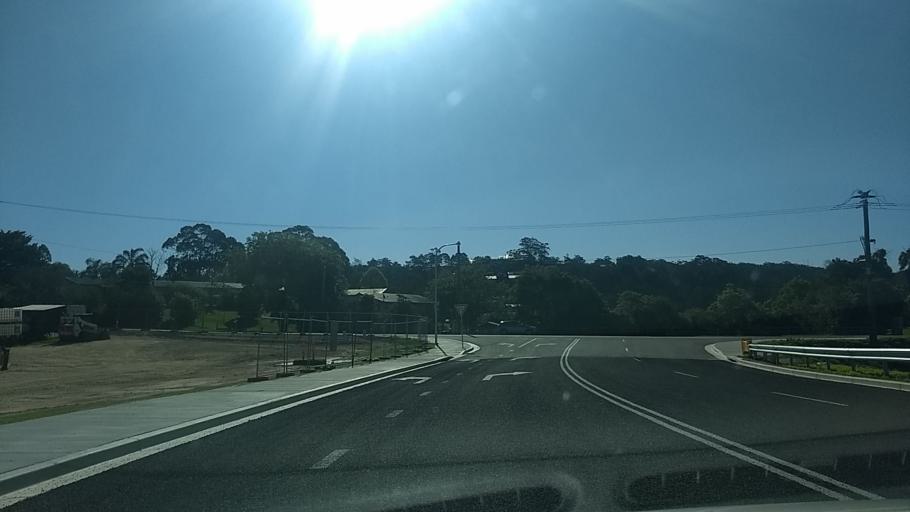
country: AU
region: New South Wales
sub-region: Bega Valley
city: Merimbula
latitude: -36.8851
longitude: 149.9079
